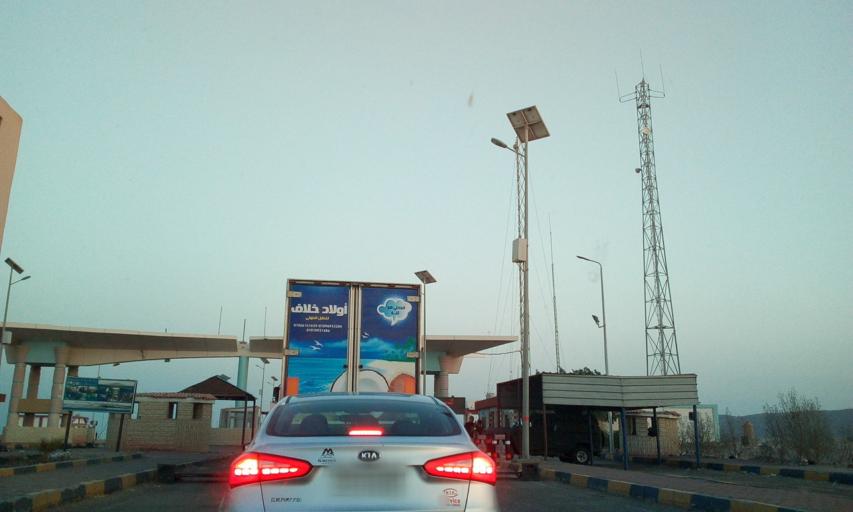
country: EG
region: Red Sea
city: El Gouna
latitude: 27.4208
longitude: 33.6151
